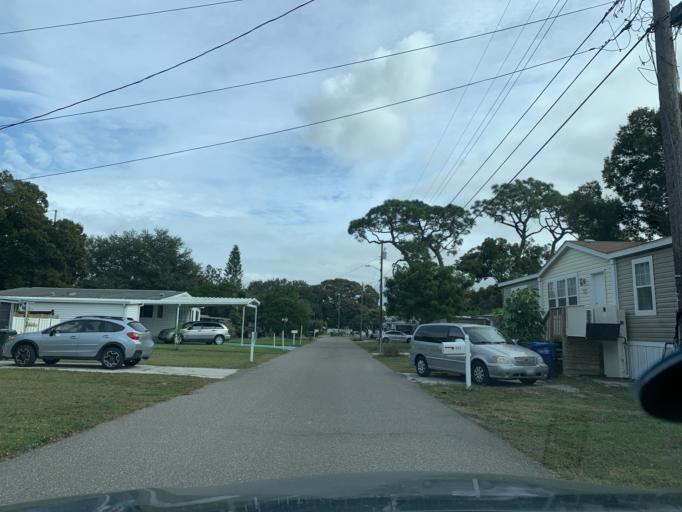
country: US
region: Florida
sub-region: Pinellas County
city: Ridgecrest
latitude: 27.8908
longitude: -82.7902
